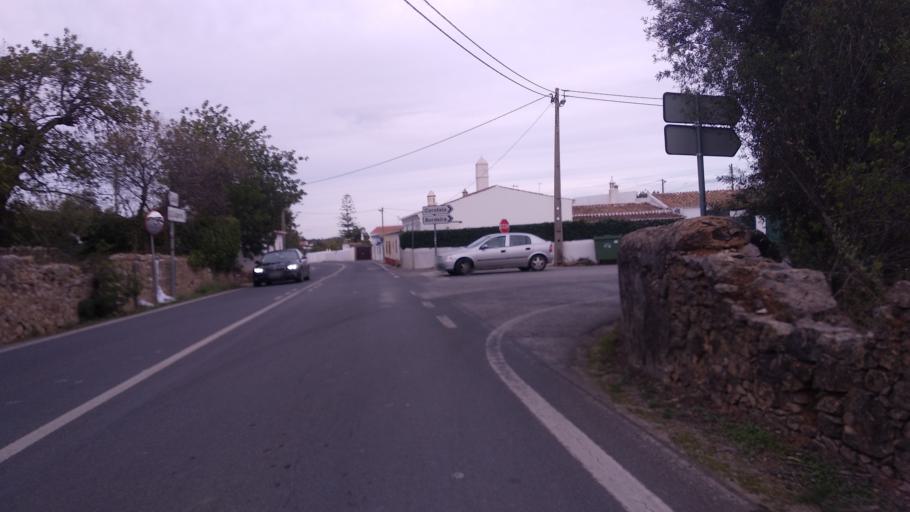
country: PT
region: Faro
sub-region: Sao Bras de Alportel
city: Sao Bras de Alportel
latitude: 37.1507
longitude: -7.9323
